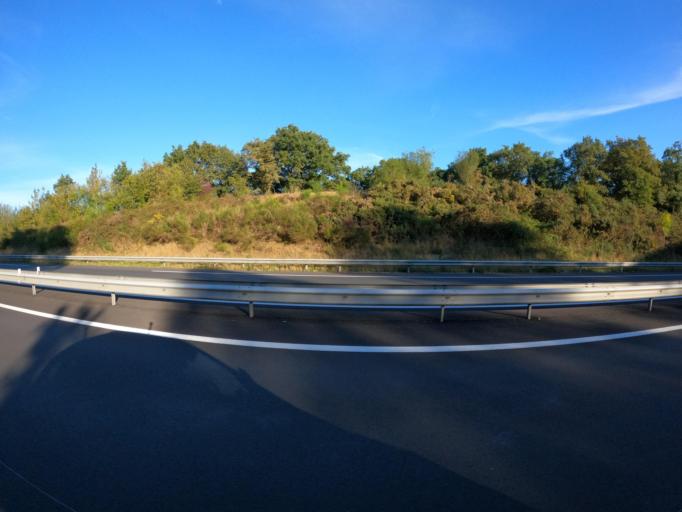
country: FR
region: Pays de la Loire
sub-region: Departement de la Vendee
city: Saint-Laurent-sur-Sevre
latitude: 46.9699
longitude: -0.9187
